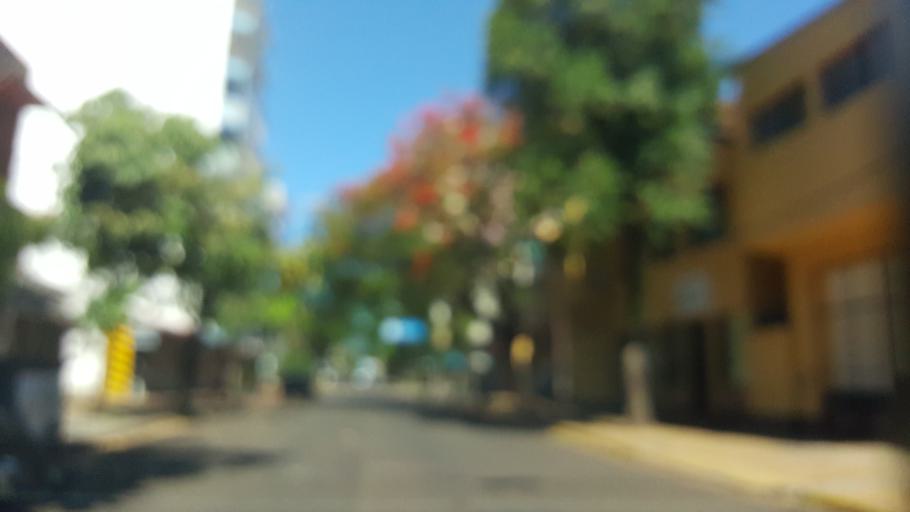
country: AR
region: Misiones
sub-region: Departamento de Capital
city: Posadas
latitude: -27.3692
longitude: -55.8991
